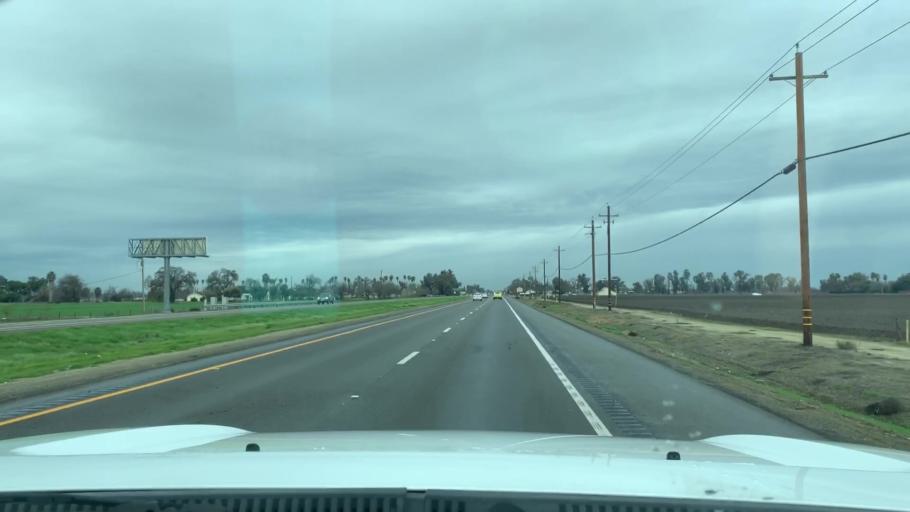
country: US
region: California
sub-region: Kings County
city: Lemoore
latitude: 36.3241
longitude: -119.8078
